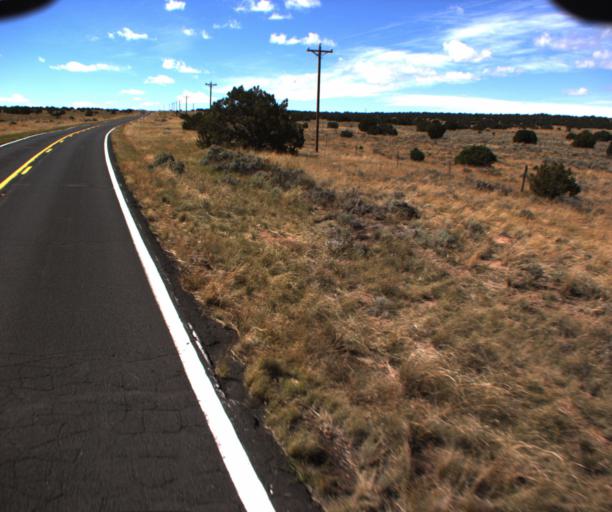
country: US
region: New Mexico
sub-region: McKinley County
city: Zuni Pueblo
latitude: 34.9749
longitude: -109.1351
